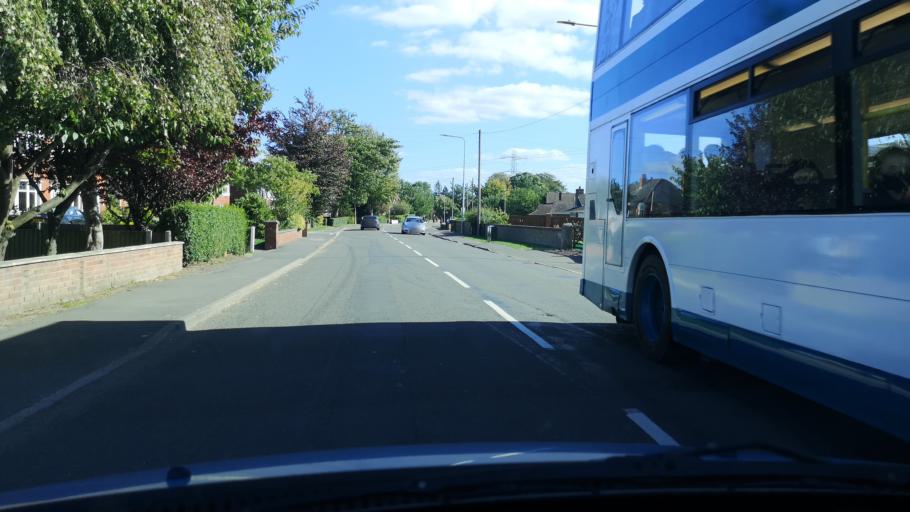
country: GB
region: England
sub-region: North Lincolnshire
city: Crowle
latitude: 53.6025
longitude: -0.8304
